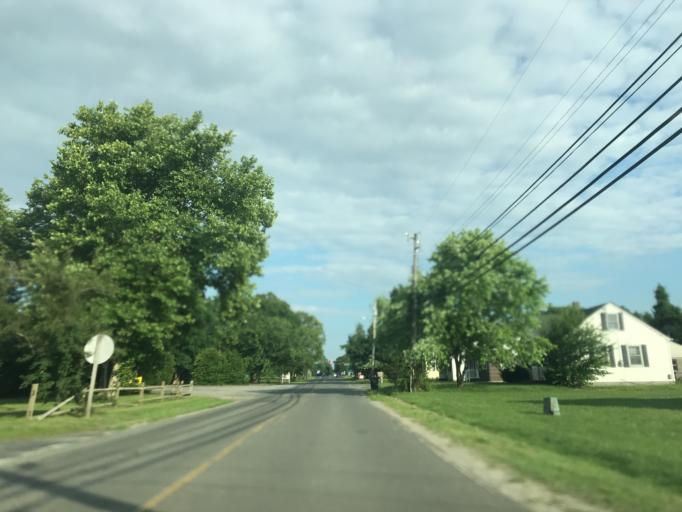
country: US
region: Maryland
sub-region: Caroline County
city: Federalsburg
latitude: 38.6911
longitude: -75.7671
